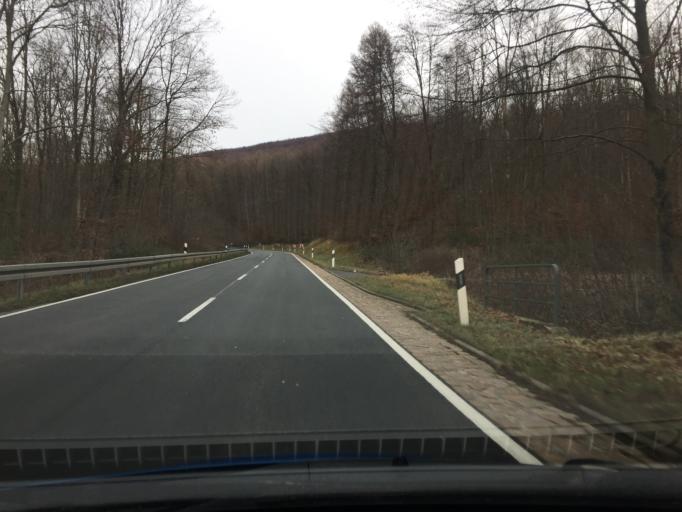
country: DE
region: Lower Saxony
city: Luerdissen
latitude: 51.9564
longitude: 9.6439
